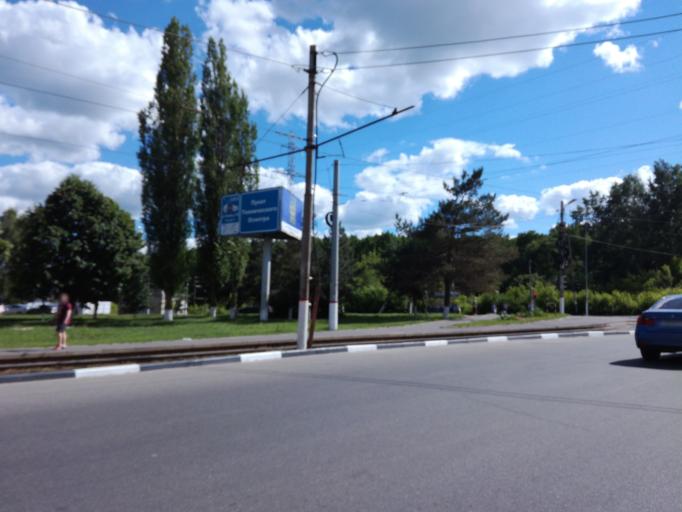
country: RU
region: Kursk
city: Kursk
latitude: 51.7541
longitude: 36.2132
